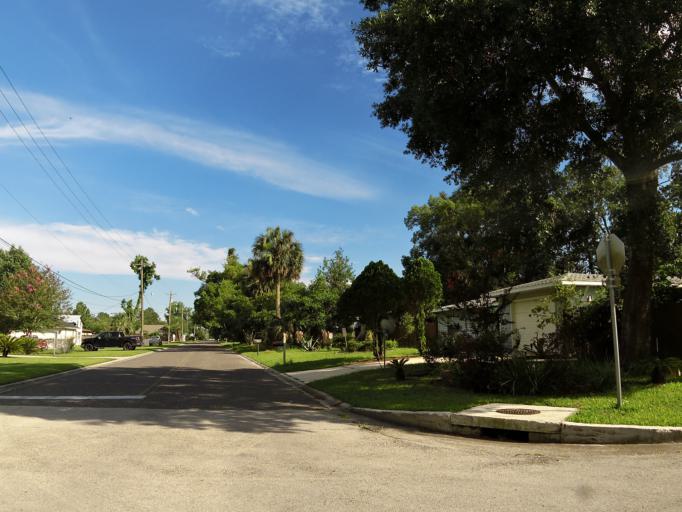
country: US
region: Florida
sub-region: Clay County
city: Green Cove Springs
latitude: 29.9883
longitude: -81.6937
